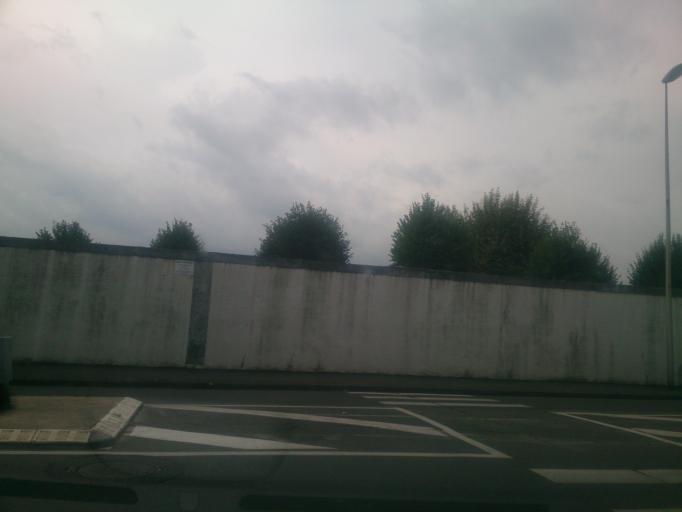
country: FR
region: Midi-Pyrenees
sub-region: Departement des Hautes-Pyrenees
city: Tarbes
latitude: 43.2287
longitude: 0.0737
